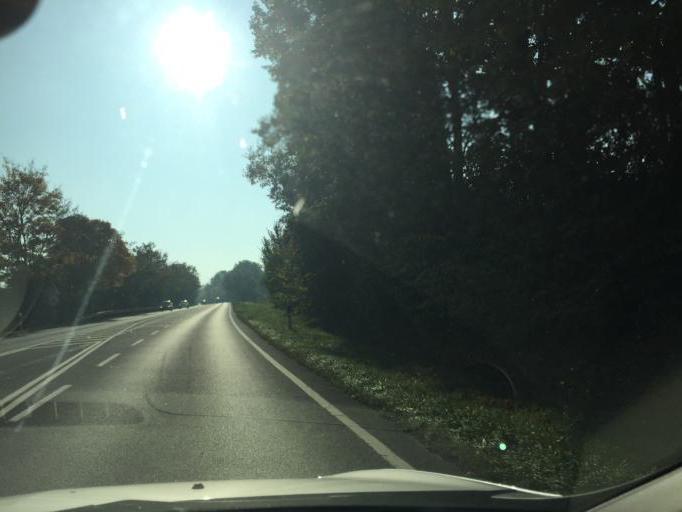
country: LU
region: Grevenmacher
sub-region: Canton de Remich
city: Bous
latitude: 49.5519
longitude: 6.3369
